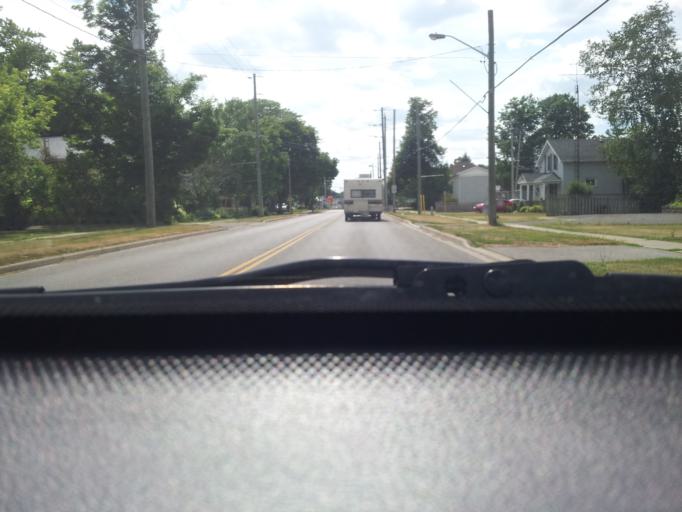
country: CA
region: Ontario
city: Brant
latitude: 43.1043
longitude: -80.4231
